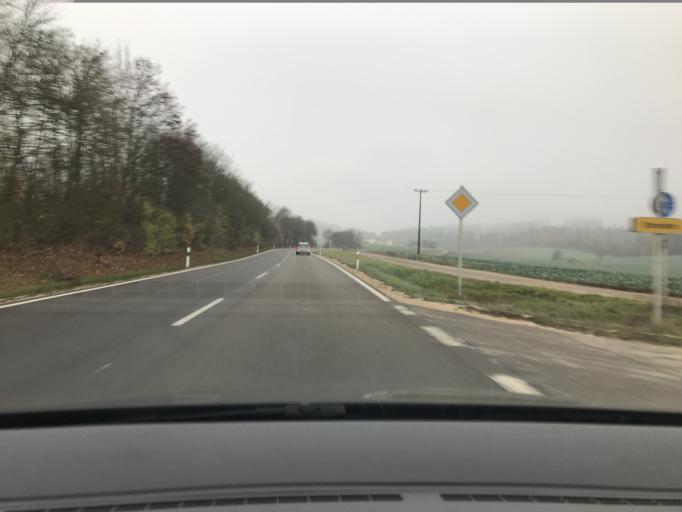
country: DE
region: Bavaria
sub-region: Swabia
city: Fremdingen
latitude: 48.9835
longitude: 10.4373
